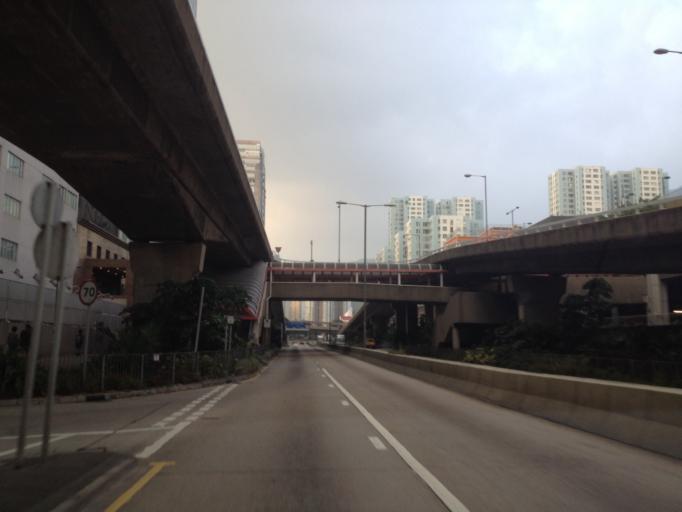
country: HK
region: Kowloon City
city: Kowloon
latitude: 22.3220
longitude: 114.2116
